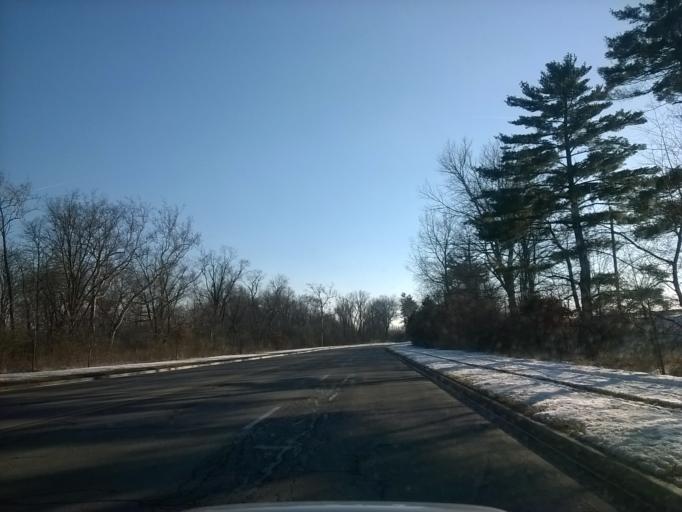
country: US
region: Indiana
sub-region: Hamilton County
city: Carmel
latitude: 39.9342
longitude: -86.0761
